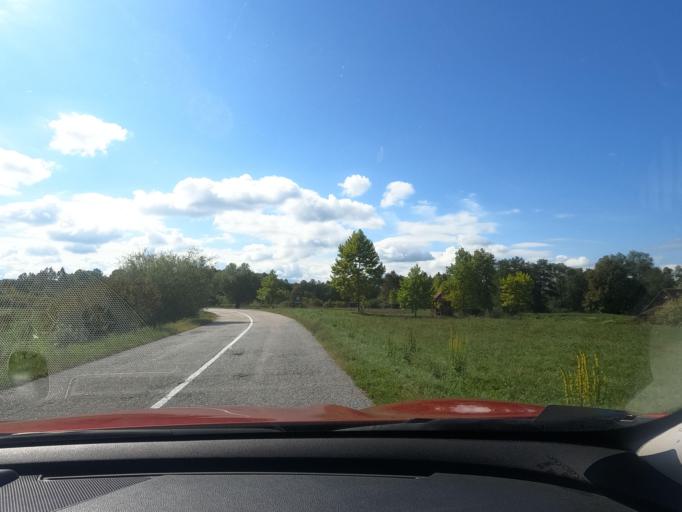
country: BA
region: Federation of Bosnia and Herzegovina
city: Vrnograc
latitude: 45.2485
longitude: 15.9416
